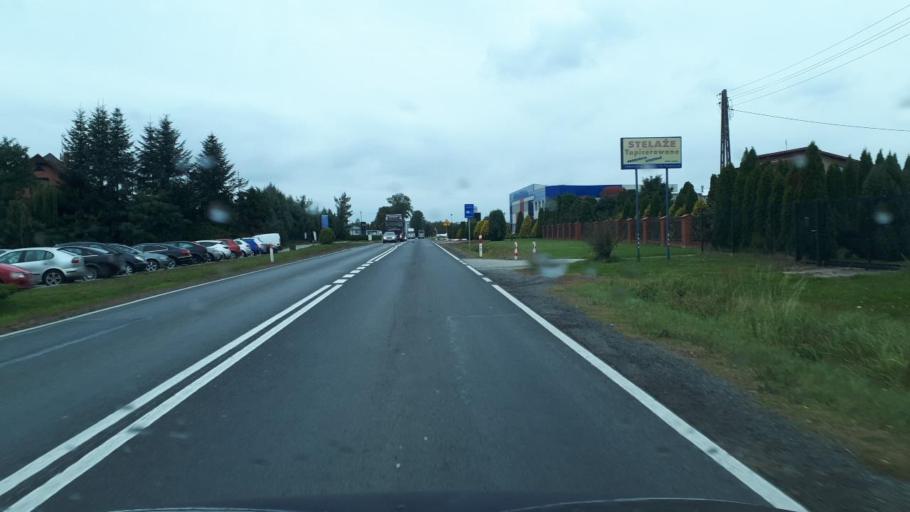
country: PL
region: Greater Poland Voivodeship
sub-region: Powiat kepinski
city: Leka Opatowska
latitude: 51.2280
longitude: 18.0811
